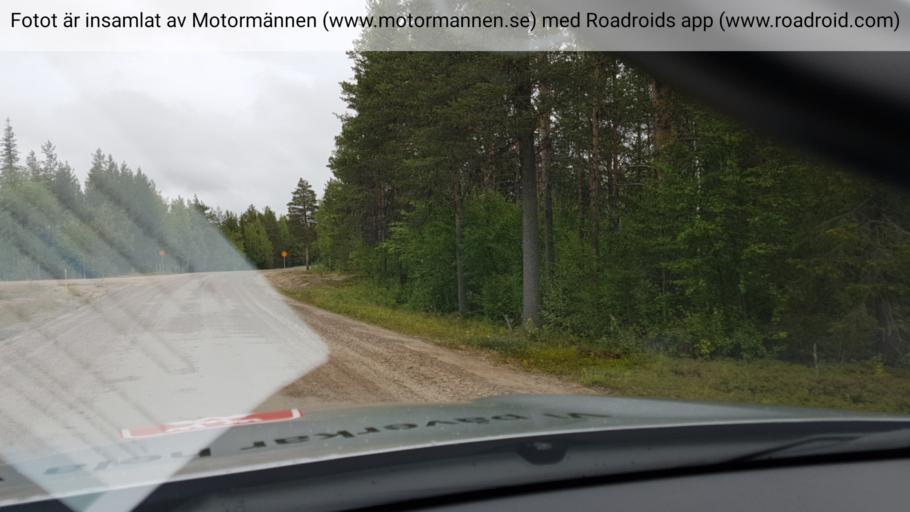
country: SE
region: Norrbotten
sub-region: Gallivare Kommun
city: Gaellivare
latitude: 66.7496
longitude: 20.9379
